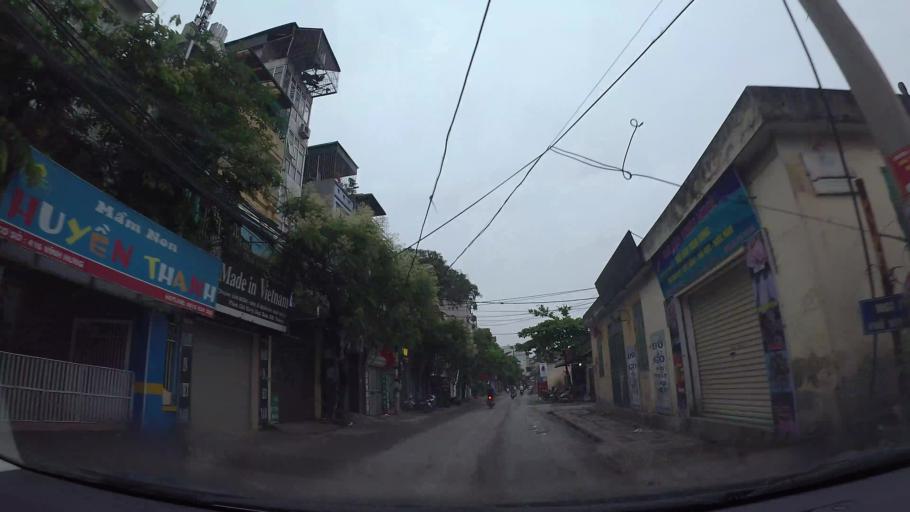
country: VN
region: Ha Noi
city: Hai BaTrung
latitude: 20.9957
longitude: 105.8800
